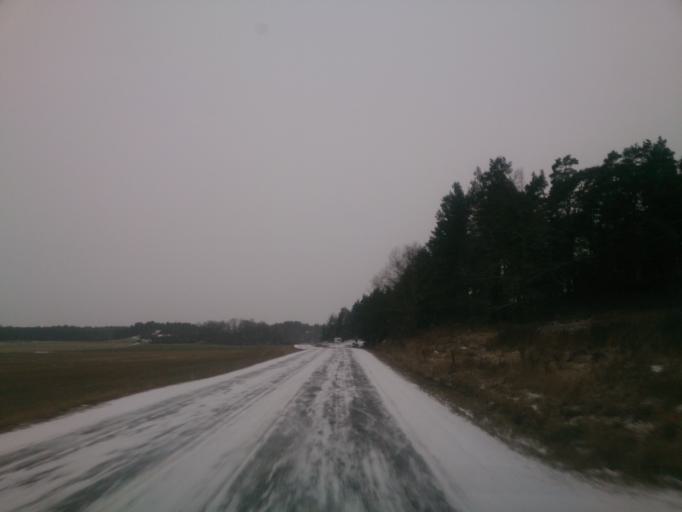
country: SE
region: OEstergoetland
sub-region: Norrkopings Kommun
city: Kimstad
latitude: 58.4811
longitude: 15.9701
